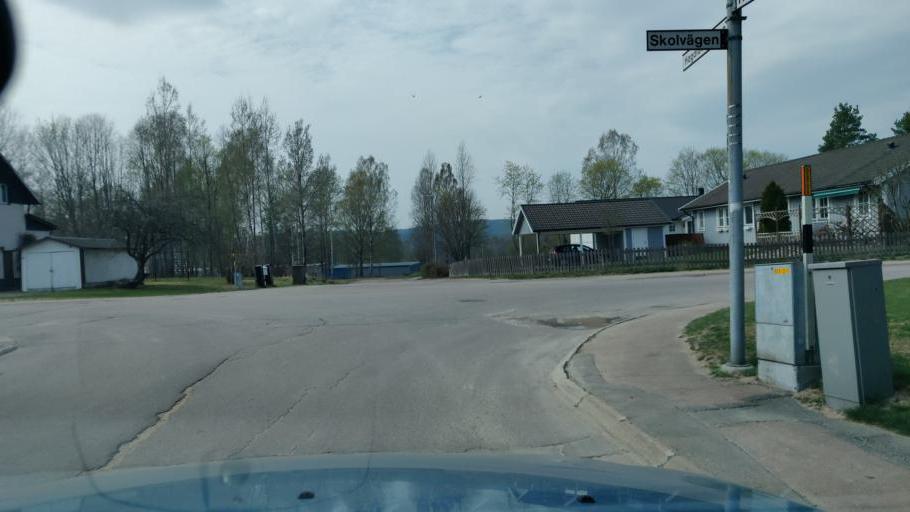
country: SE
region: Vaermland
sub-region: Munkfors Kommun
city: Munkfors
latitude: 59.8447
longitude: 13.5592
